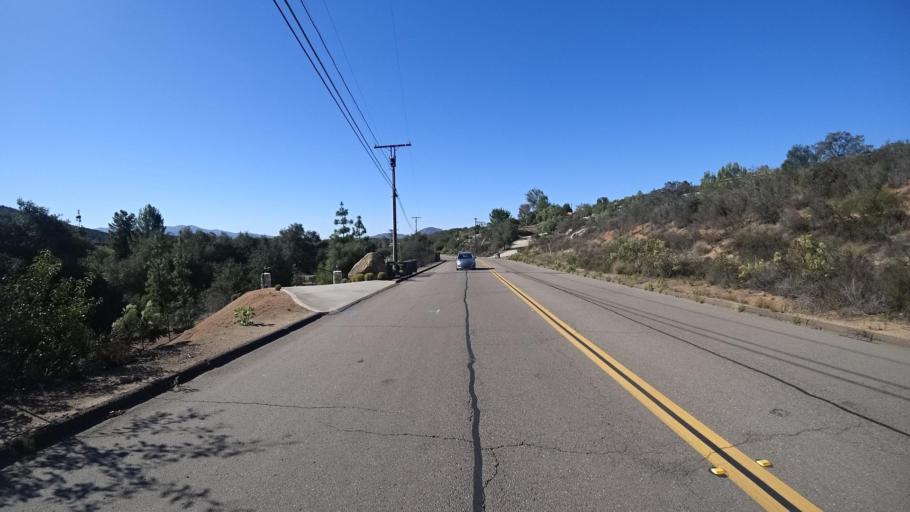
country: US
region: California
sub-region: San Diego County
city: Jamul
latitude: 32.7257
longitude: -116.8445
